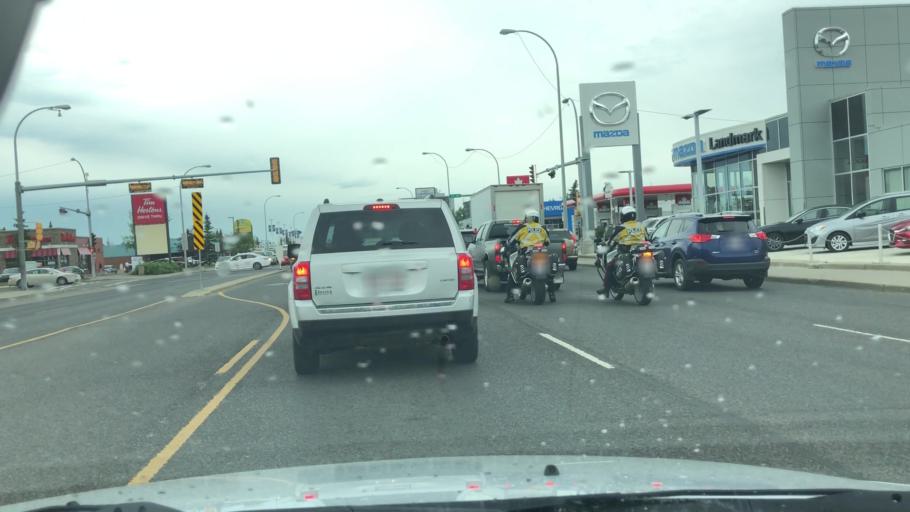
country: CA
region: Alberta
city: Edmonton
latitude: 53.5915
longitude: -113.4920
